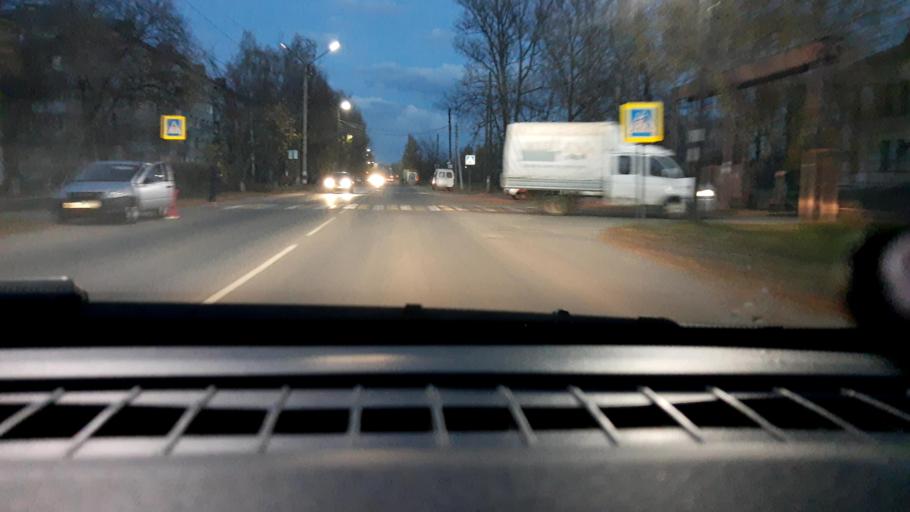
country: RU
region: Nizjnij Novgorod
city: Novaya Balakhna
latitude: 56.4872
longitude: 43.5832
